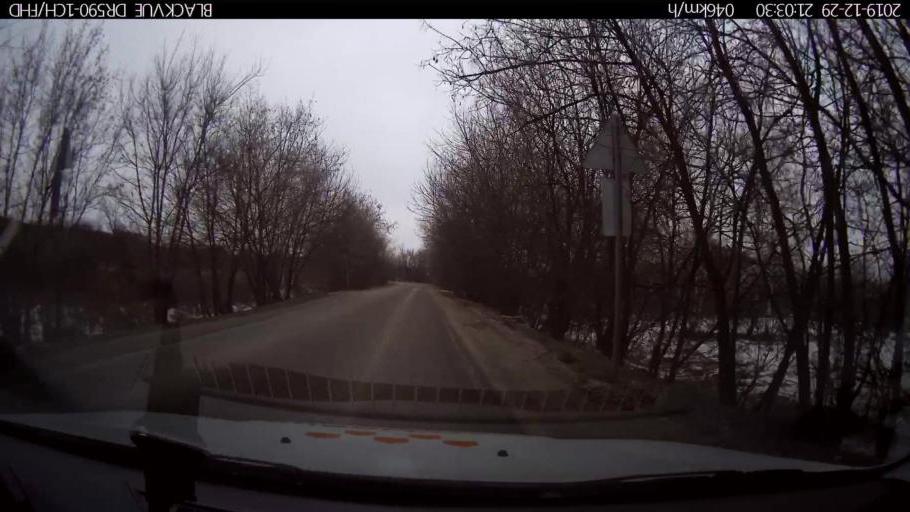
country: RU
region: Nizjnij Novgorod
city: Afonino
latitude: 56.1957
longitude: 44.0058
